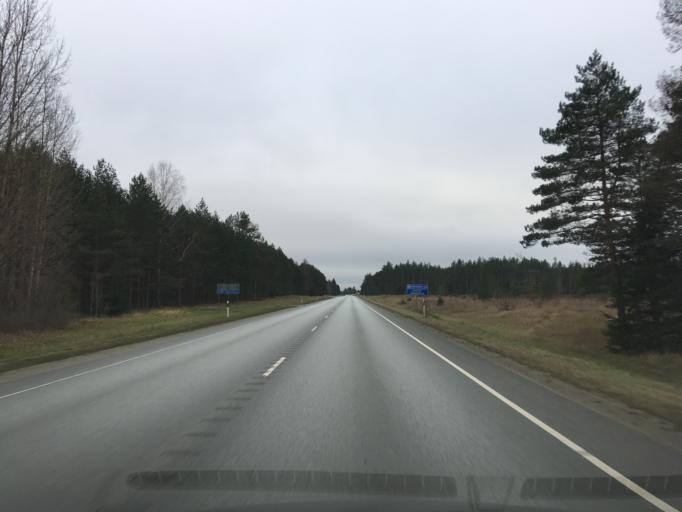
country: EE
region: Laeaene-Virumaa
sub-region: Viru-Nigula vald
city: Kunda
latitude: 59.4011
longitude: 26.6311
